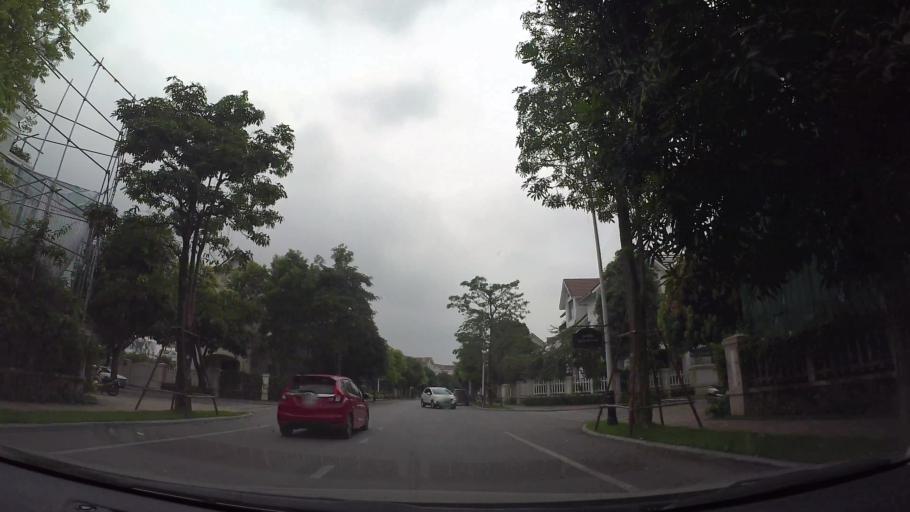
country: VN
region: Ha Noi
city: Trau Quy
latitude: 21.0404
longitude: 105.9193
